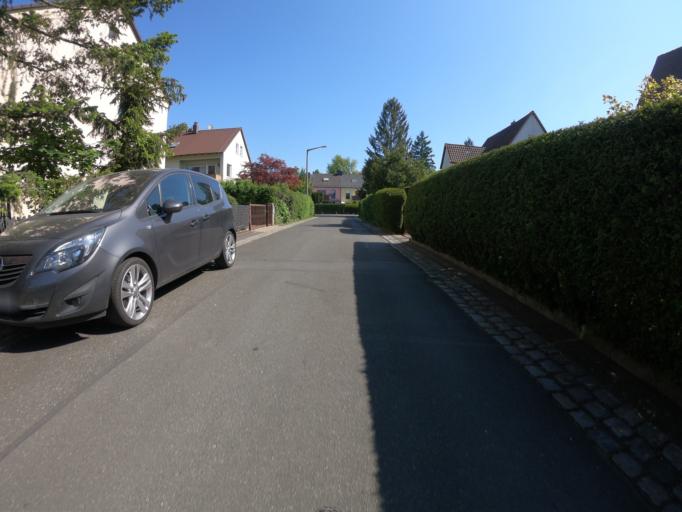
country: DE
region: Bavaria
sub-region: Regierungsbezirk Mittelfranken
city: Stein
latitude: 49.4085
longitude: 11.0262
